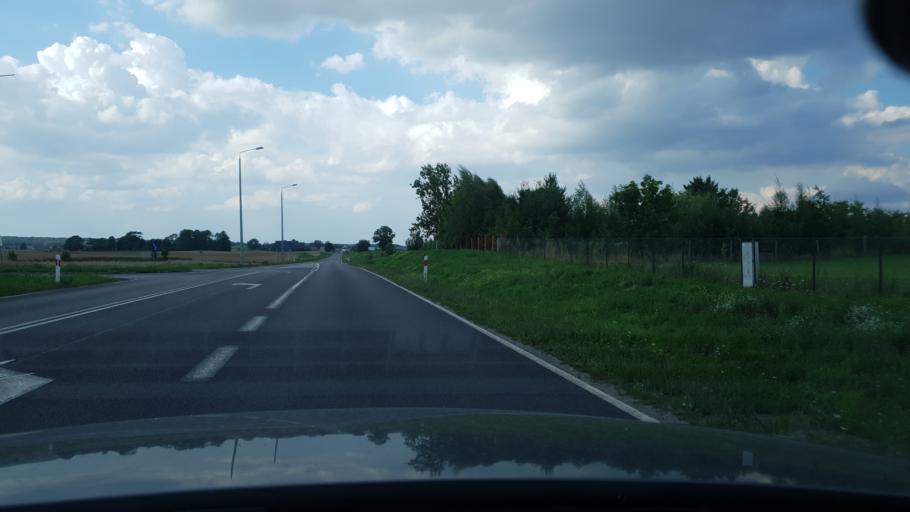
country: PL
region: Kujawsko-Pomorskie
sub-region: Powiat wabrzeski
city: Wabrzezno
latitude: 53.2867
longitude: 18.9279
